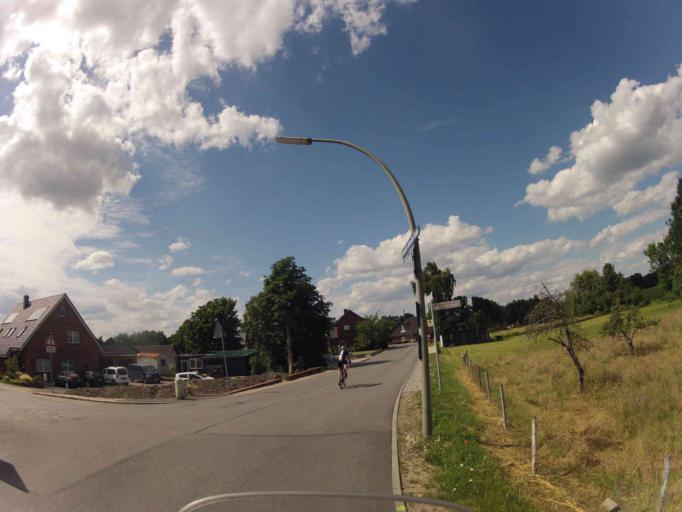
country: DE
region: Lower Saxony
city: Stelle
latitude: 53.4559
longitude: 10.1420
